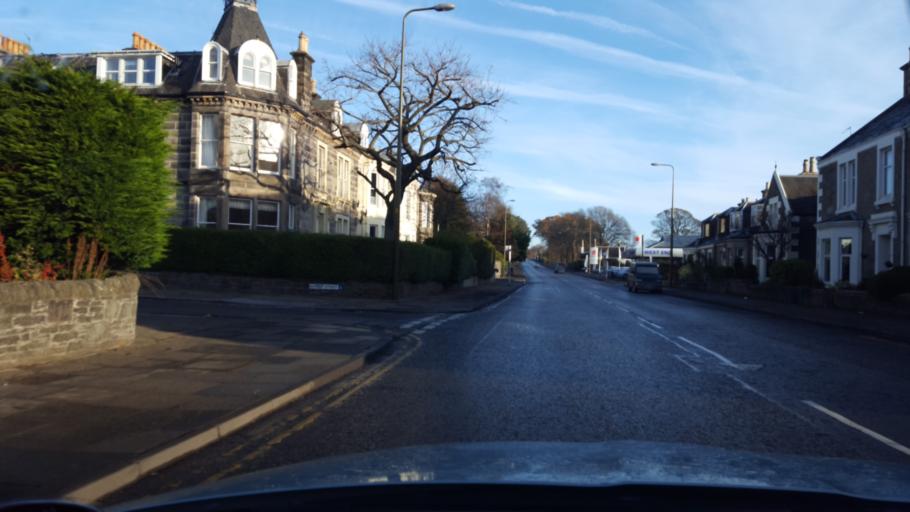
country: GB
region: Scotland
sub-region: Fife
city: Tayport
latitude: 56.4682
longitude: -2.8649
